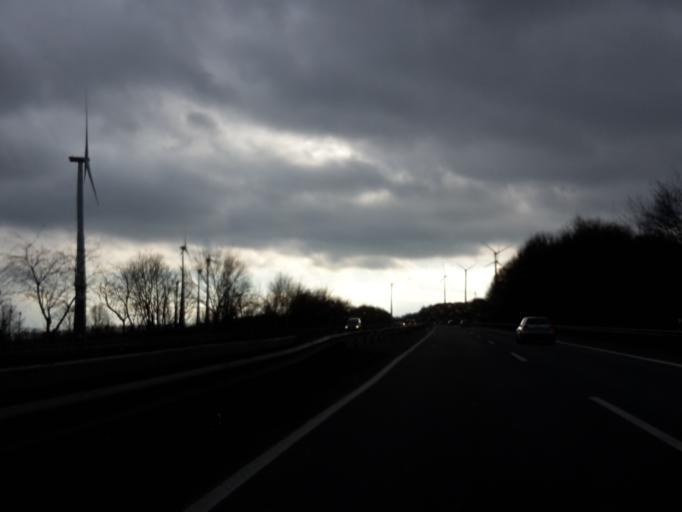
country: DE
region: Rheinland-Pfalz
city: Ober-Saulheim
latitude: 49.8497
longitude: 8.1476
